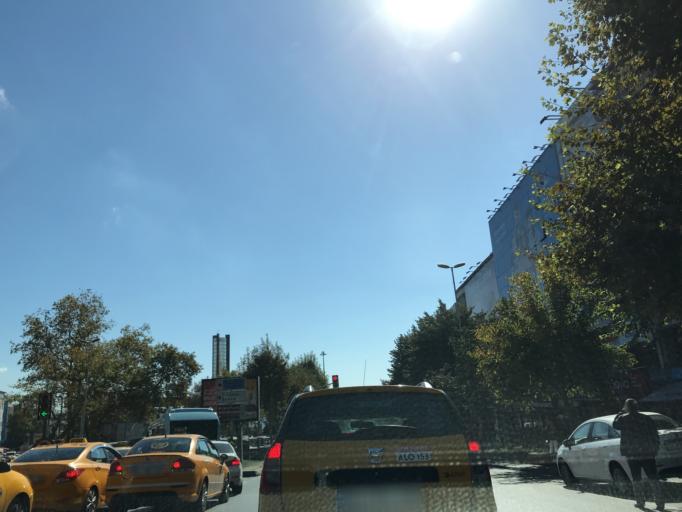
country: TR
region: Istanbul
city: Sisli
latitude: 41.0445
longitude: 29.0072
